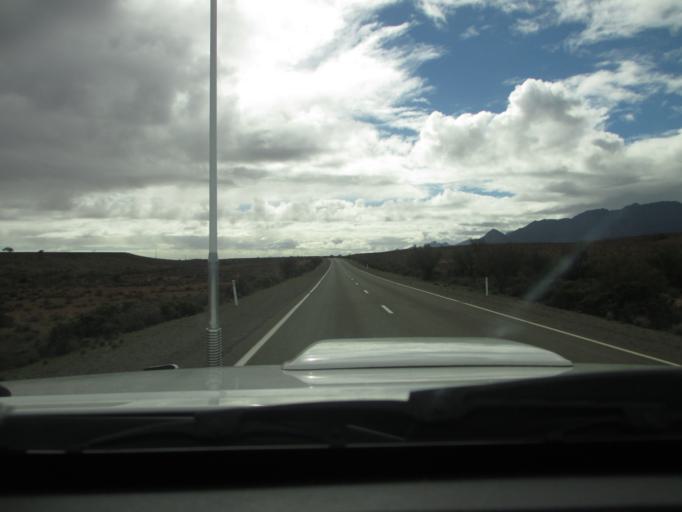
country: AU
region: South Australia
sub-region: Flinders Ranges
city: Quorn
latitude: -31.5679
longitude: 138.4262
